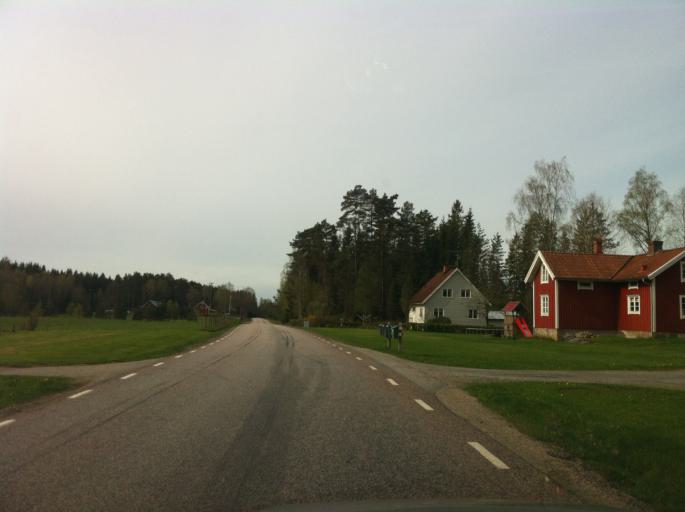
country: SE
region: Vaestra Goetaland
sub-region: Bollebygds Kommun
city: Bollebygd
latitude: 57.5888
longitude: 12.5788
